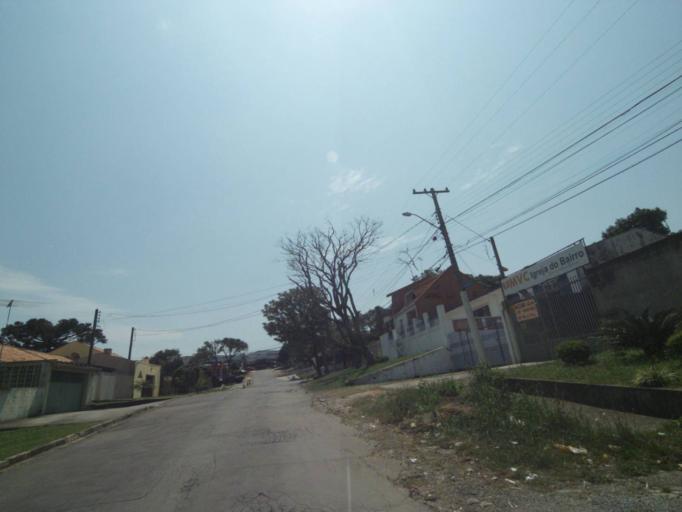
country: BR
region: Parana
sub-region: Curitiba
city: Curitiba
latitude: -25.4802
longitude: -49.3128
